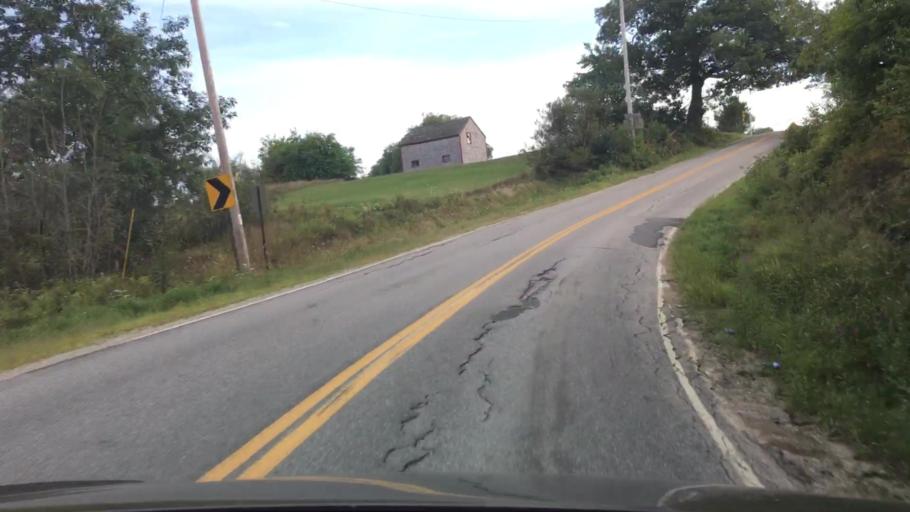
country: US
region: Maine
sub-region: Hancock County
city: Penobscot
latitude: 44.4691
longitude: -68.7390
